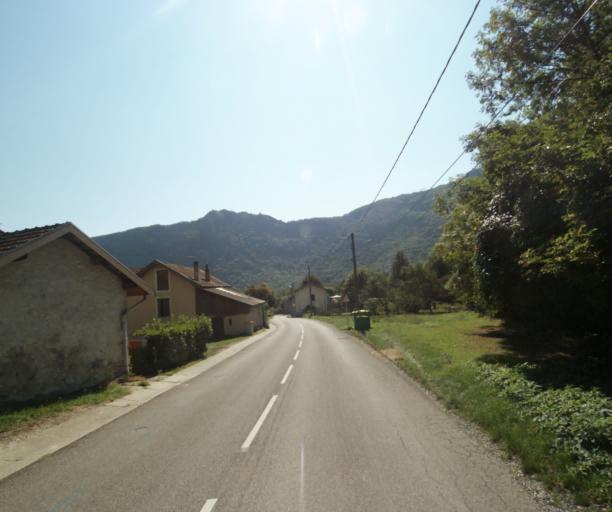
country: FR
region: Rhone-Alpes
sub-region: Departement de l'Isere
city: Saint-Paul-de-Varces
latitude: 45.0711
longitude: 5.6434
